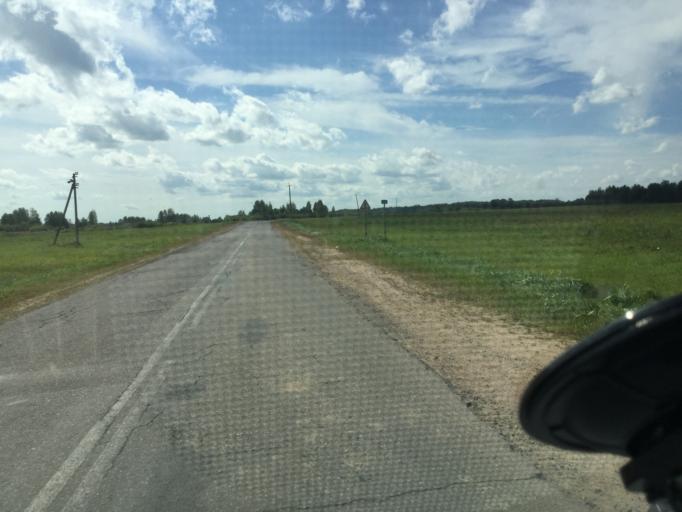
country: BY
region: Vitebsk
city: Chashniki
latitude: 55.3139
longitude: 29.4209
